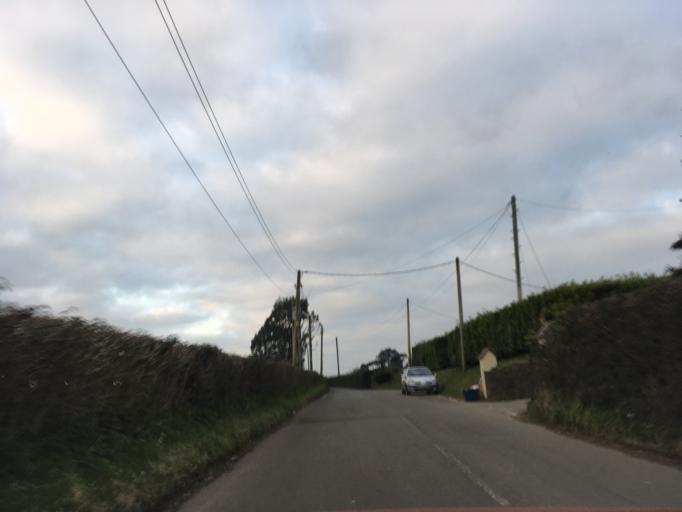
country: GB
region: Wales
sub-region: Newport
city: Marshfield
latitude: 51.5508
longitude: -3.0937
